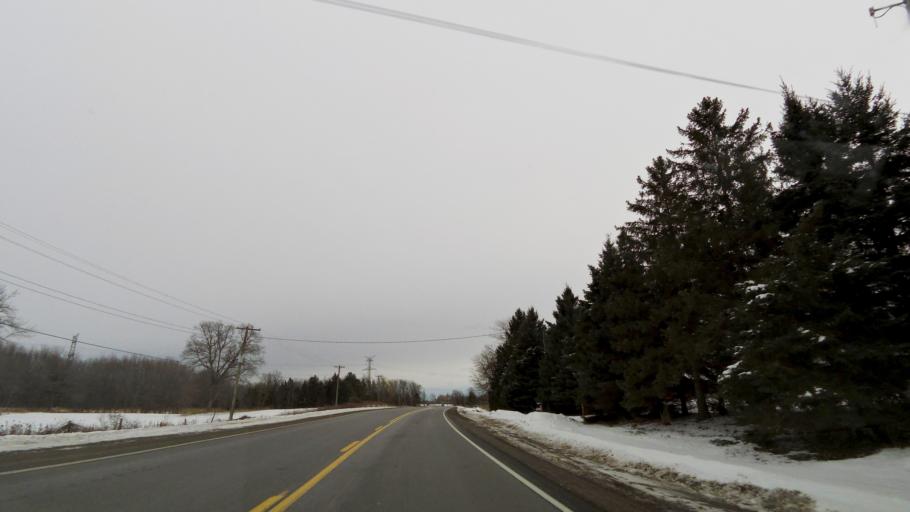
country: CA
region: Ontario
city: Ancaster
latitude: 43.2897
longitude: -80.0929
